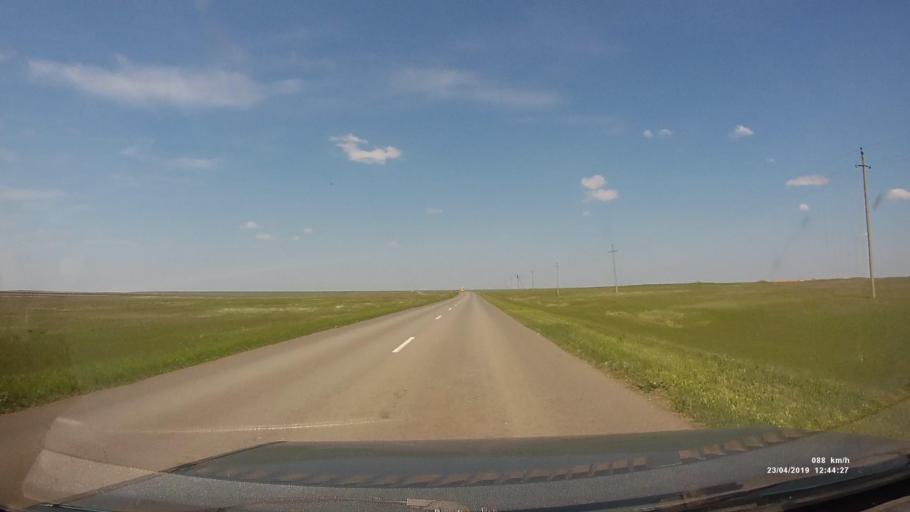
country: RU
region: Kalmykiya
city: Yashalta
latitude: 46.4769
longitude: 42.6474
